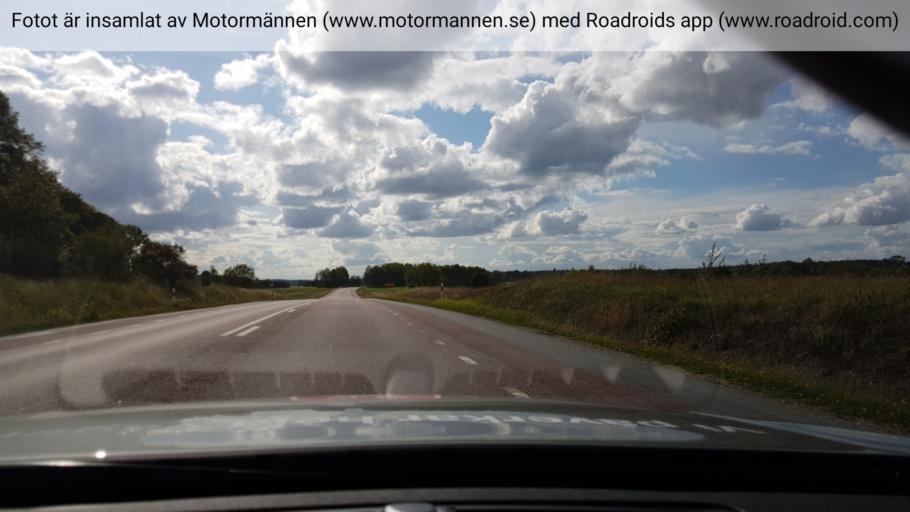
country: SE
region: Uppsala
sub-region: Enkopings Kommun
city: Grillby
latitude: 59.6597
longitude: 17.2218
